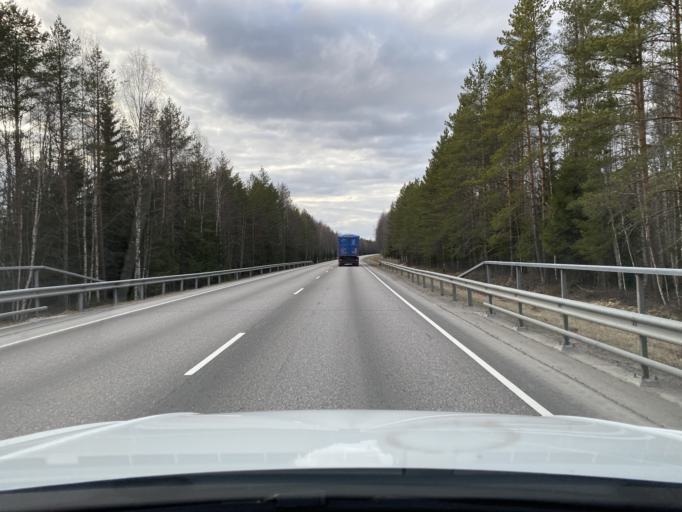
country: FI
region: Uusimaa
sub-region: Helsinki
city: Kaerkoelae
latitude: 60.8108
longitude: 24.0577
